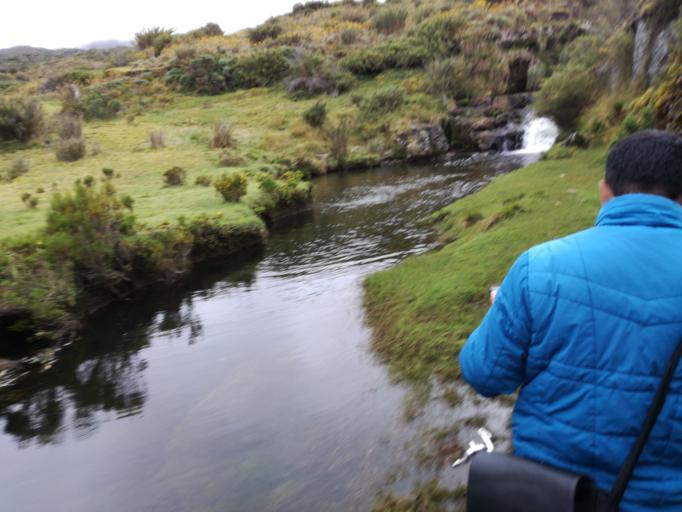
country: CO
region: Boyaca
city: Socha Viejo
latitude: 5.8897
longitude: -72.6760
